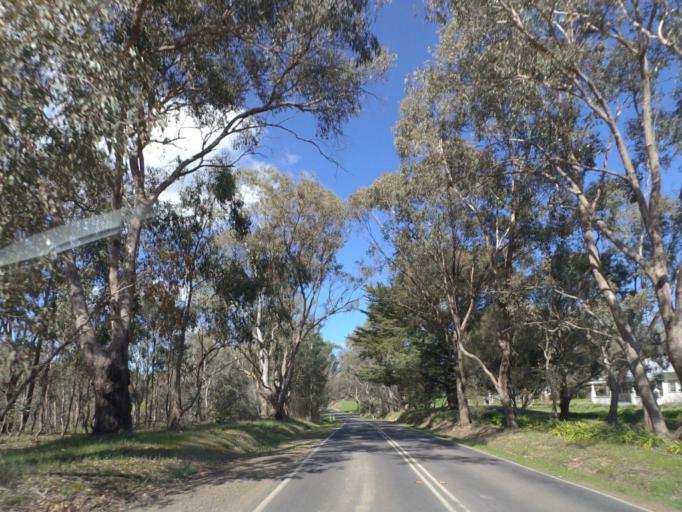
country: AU
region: Victoria
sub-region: Murrindindi
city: Alexandra
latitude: -37.1910
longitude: 145.7214
